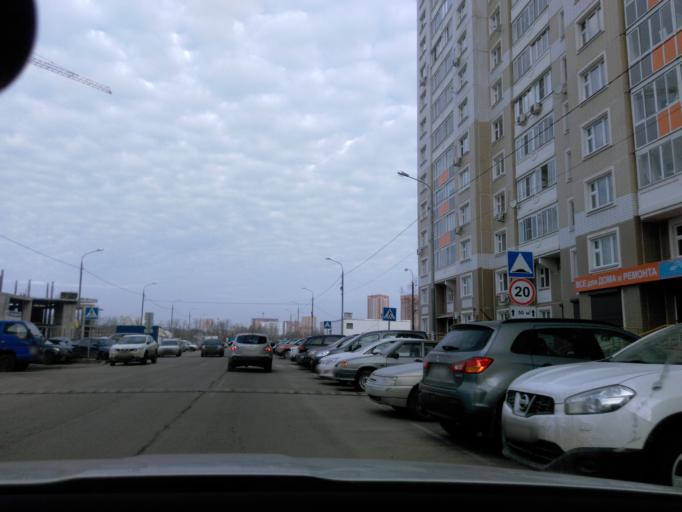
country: RU
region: Moskovskaya
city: Levoberezhnaya
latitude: 55.8986
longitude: 37.4775
